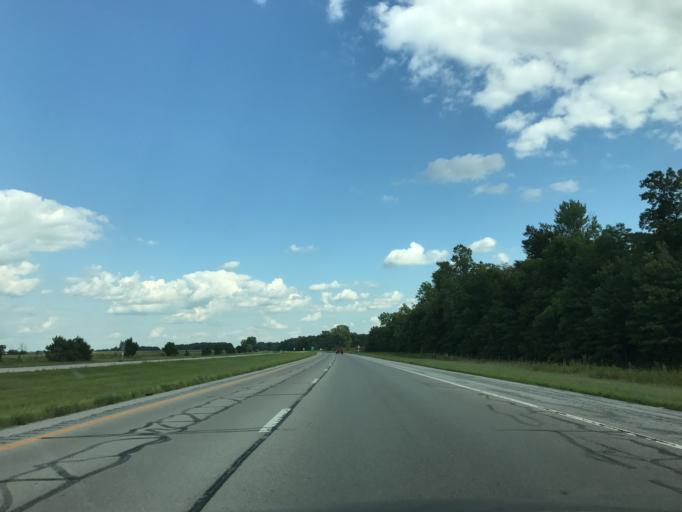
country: US
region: Ohio
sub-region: Allen County
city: Elida
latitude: 40.8248
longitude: -84.1278
